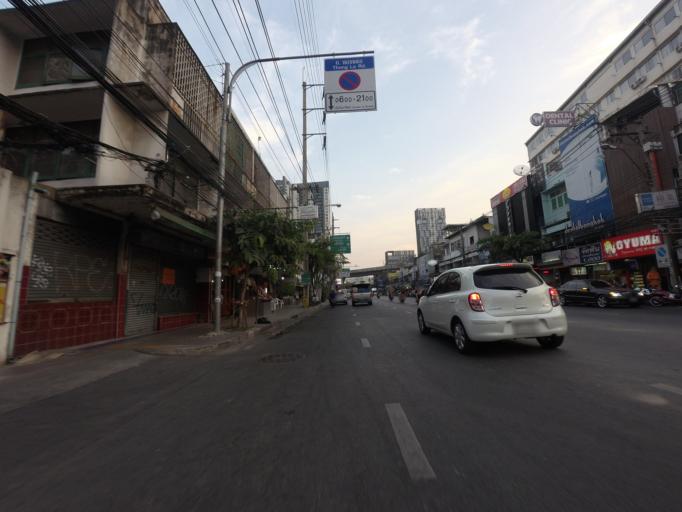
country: TH
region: Bangkok
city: Watthana
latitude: 13.7251
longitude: 100.5795
